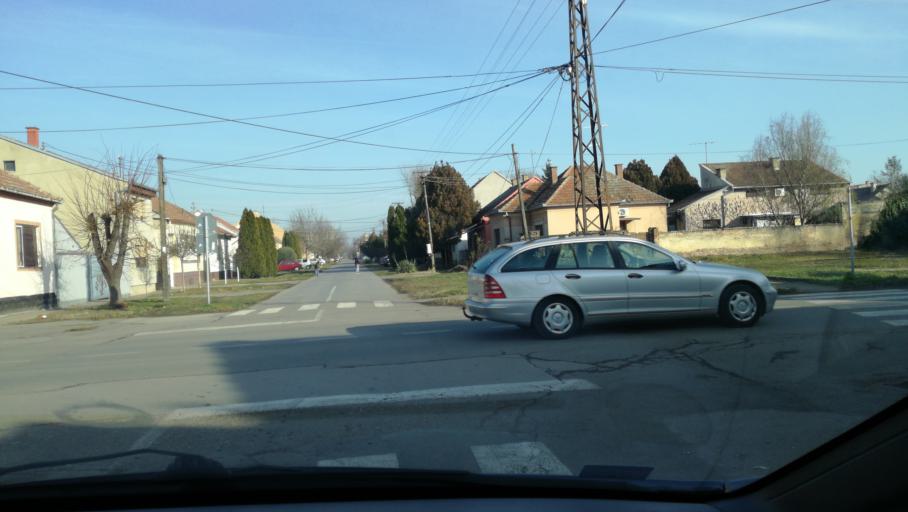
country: RS
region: Autonomna Pokrajina Vojvodina
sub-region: Severnobanatski Okrug
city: Kikinda
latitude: 45.8317
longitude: 20.4728
